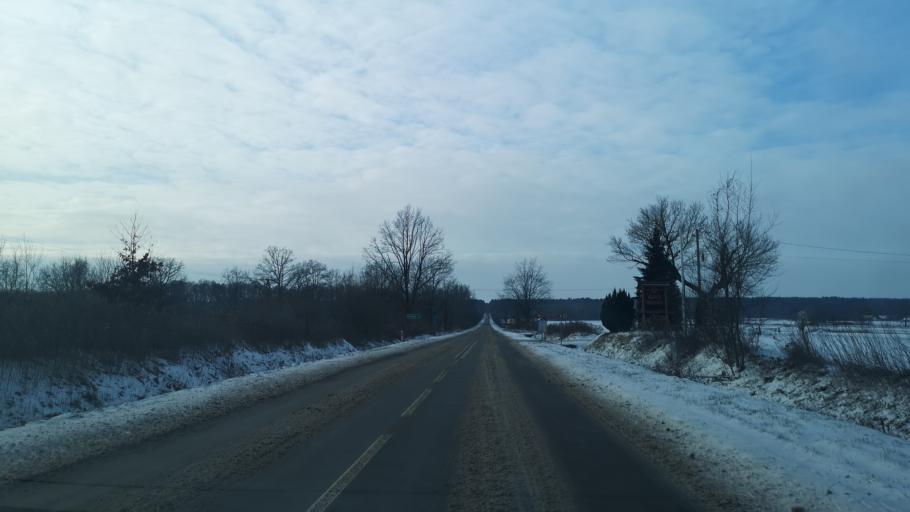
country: PL
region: Subcarpathian Voivodeship
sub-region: Powiat przeworski
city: Adamowka
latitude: 50.2263
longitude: 22.6540
